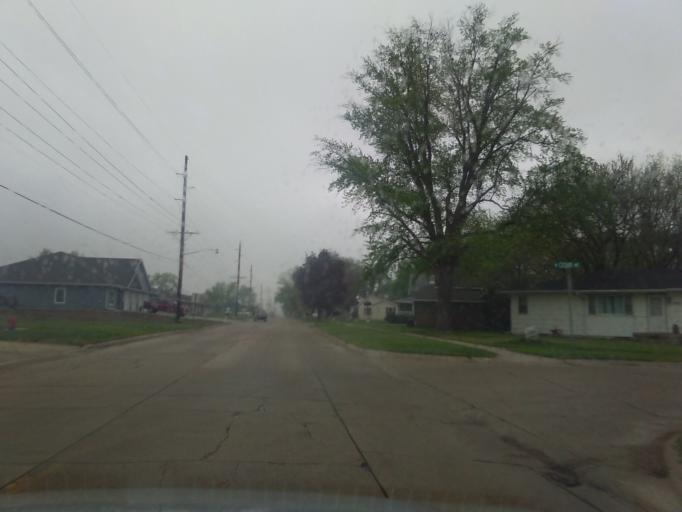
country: US
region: Nebraska
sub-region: Madison County
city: Norfolk
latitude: 42.0419
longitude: -97.4190
